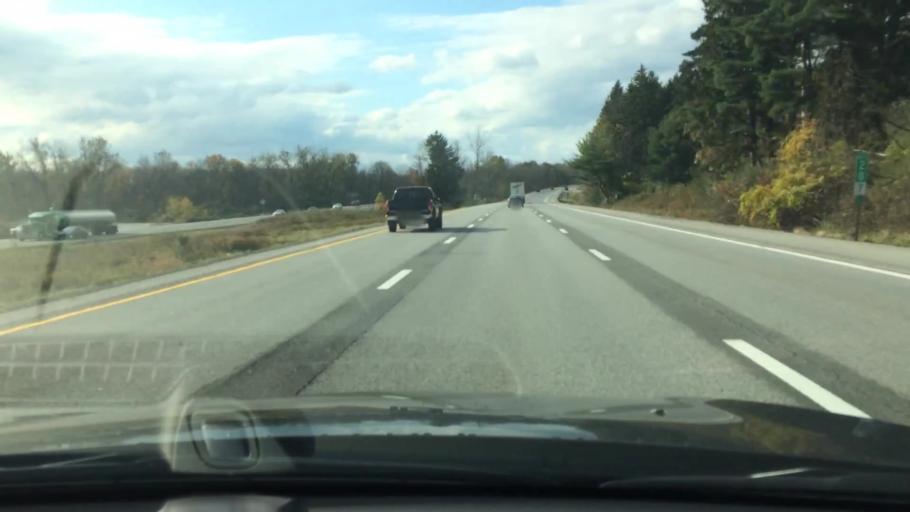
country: US
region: New York
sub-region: Saratoga County
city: Saratoga Springs
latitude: 43.0709
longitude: -73.7520
